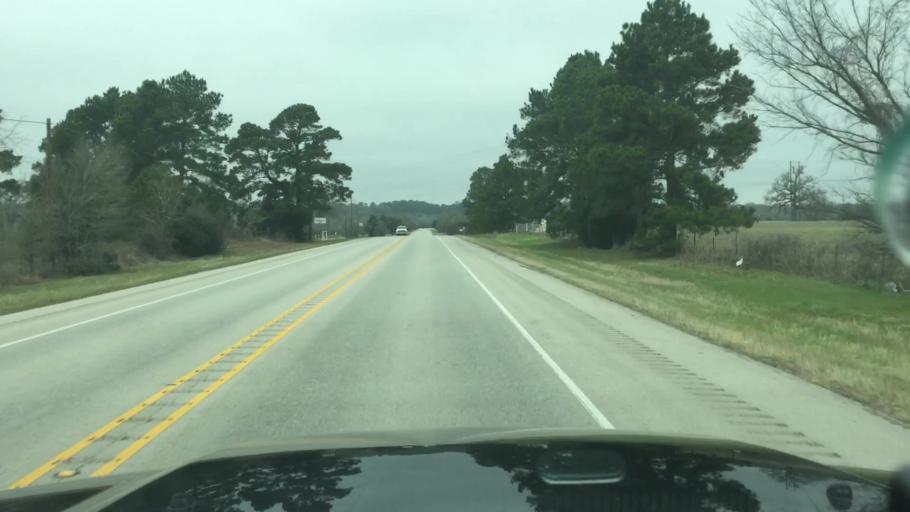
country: US
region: Texas
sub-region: Fayette County
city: La Grange
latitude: 30.0255
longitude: -96.9030
